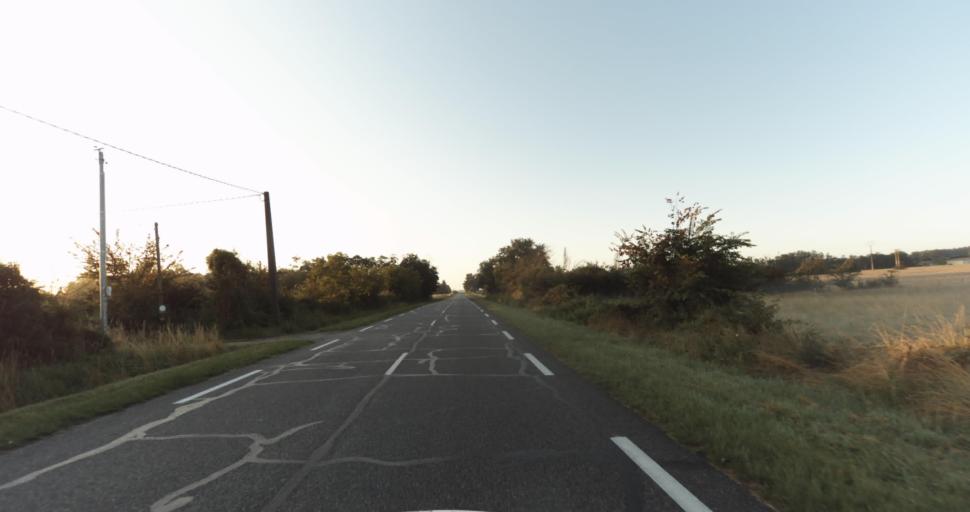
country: FR
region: Aquitaine
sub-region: Departement de la Gironde
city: Bazas
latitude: 44.4290
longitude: -0.1934
